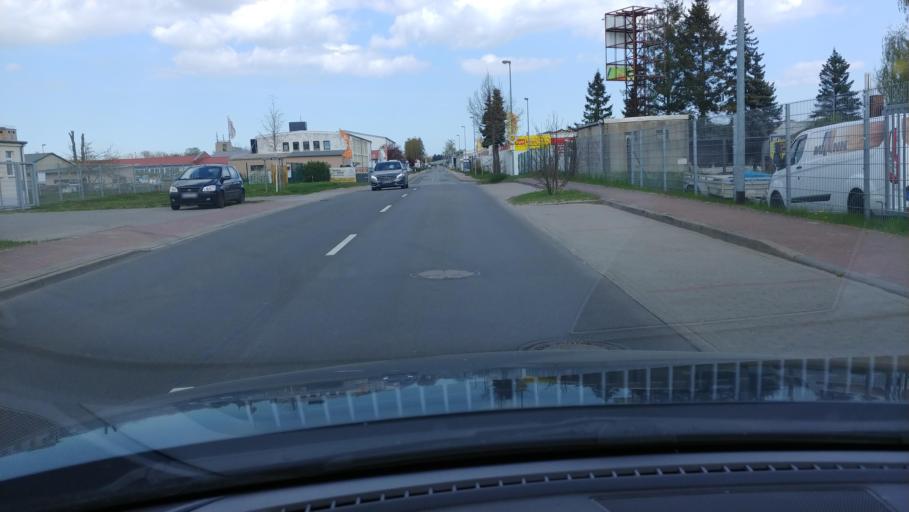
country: DE
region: Mecklenburg-Vorpommern
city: Neumuehle
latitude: 53.6031
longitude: 11.3761
